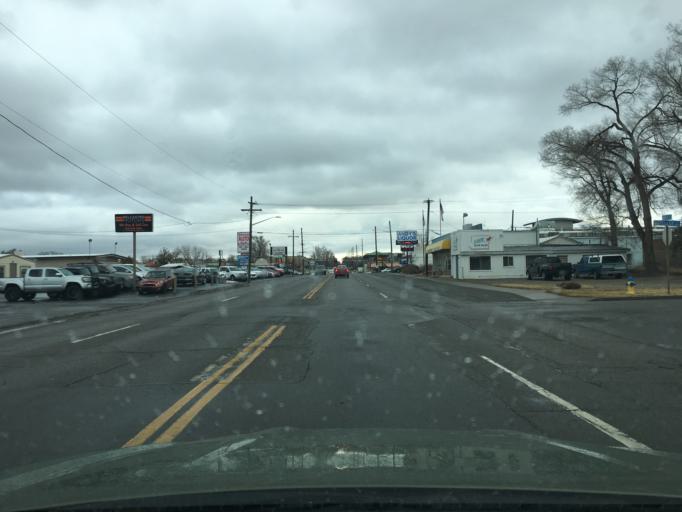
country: US
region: Colorado
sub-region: Mesa County
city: Grand Junction
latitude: 39.0753
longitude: -108.5708
